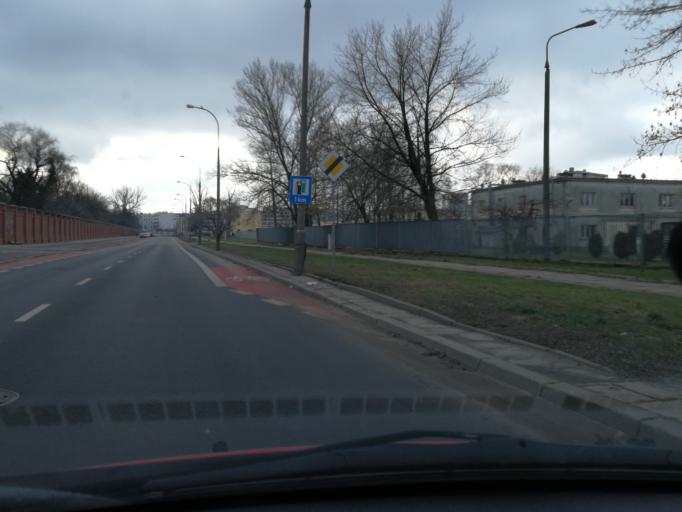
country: PL
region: Masovian Voivodeship
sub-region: Warszawa
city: Wola
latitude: 52.2523
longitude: 20.9644
